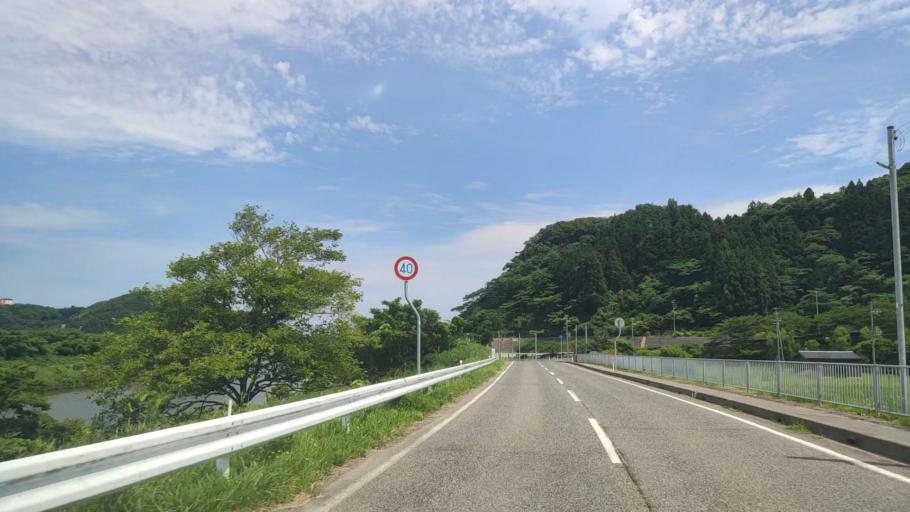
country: JP
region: Hyogo
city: Toyooka
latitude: 35.6504
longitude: 134.7637
